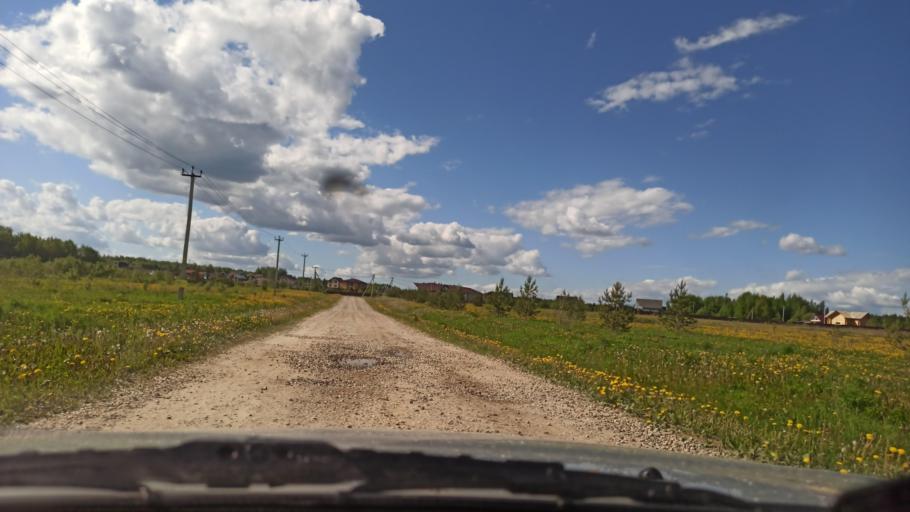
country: RU
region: Vologda
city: Molochnoye
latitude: 59.3723
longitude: 39.6947
